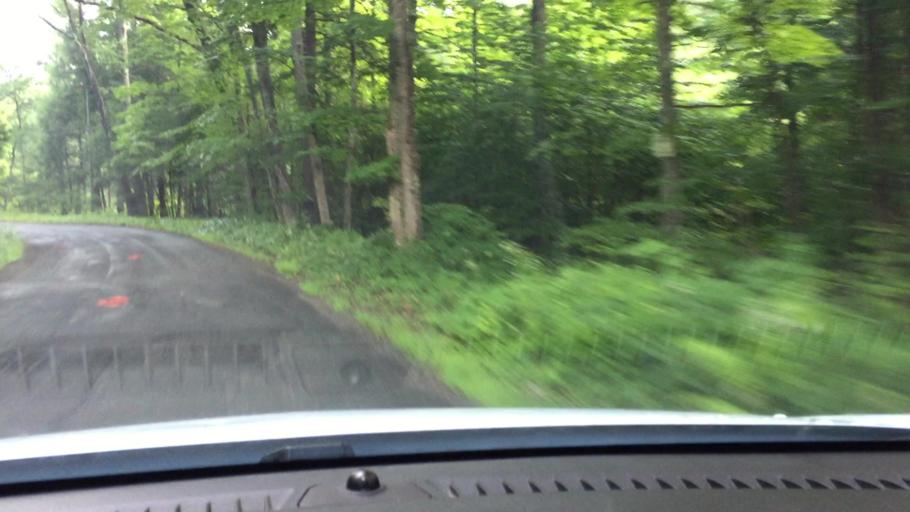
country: US
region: Massachusetts
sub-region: Hampshire County
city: Chesterfield
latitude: 42.3063
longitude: -72.9091
